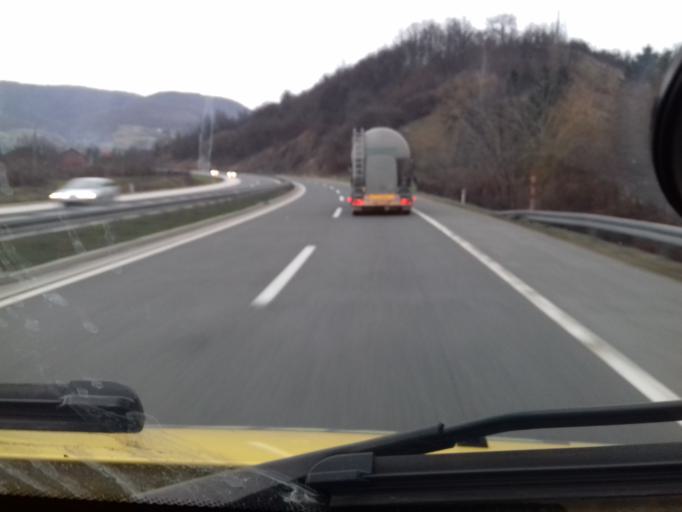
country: BA
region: Federation of Bosnia and Herzegovina
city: Ilijas
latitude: 43.9371
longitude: 18.2781
